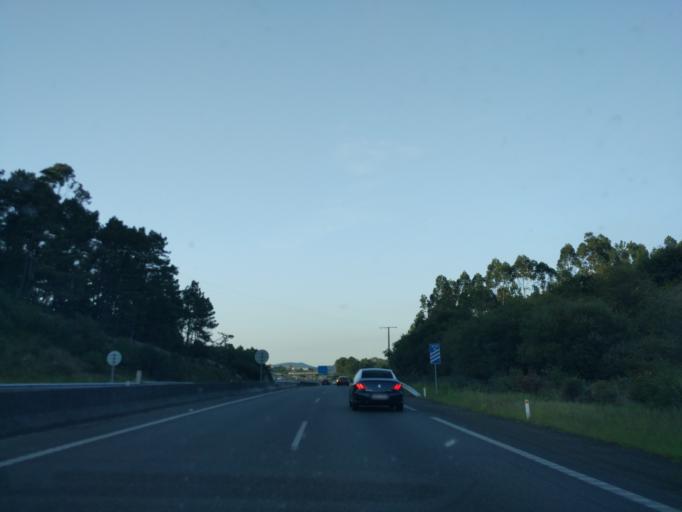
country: ES
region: Galicia
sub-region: Provincia de Pontevedra
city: Caldas de Reis
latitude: 42.6396
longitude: -8.6558
